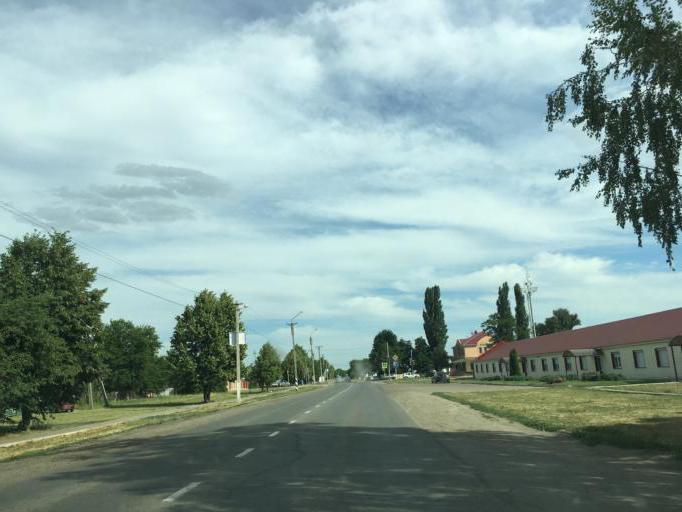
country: RU
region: Krasnodarskiy
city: Kushchevskaya
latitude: 46.5483
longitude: 39.6178
